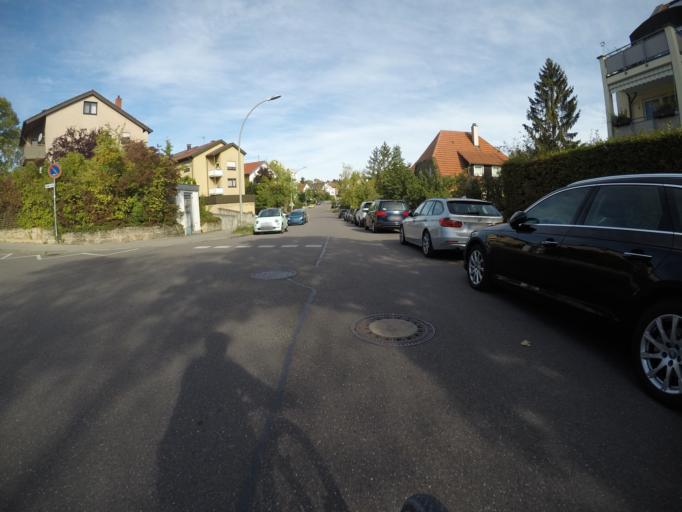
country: DE
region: Baden-Wuerttemberg
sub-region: Regierungsbezirk Stuttgart
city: Korntal
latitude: 48.8307
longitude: 9.1162
